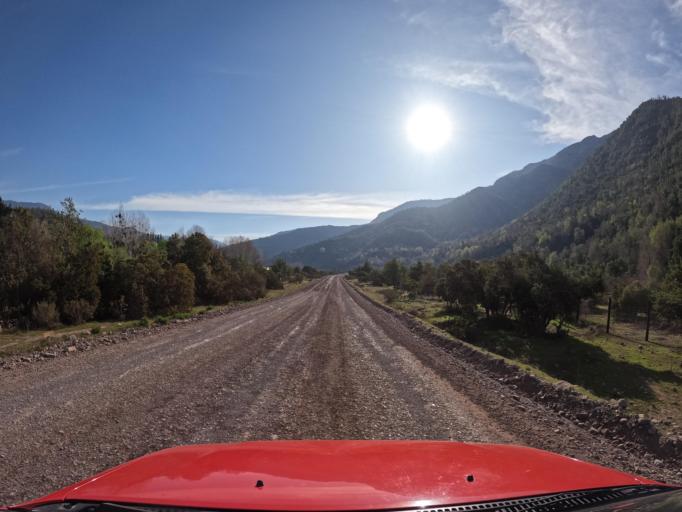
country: CL
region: O'Higgins
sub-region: Provincia de Colchagua
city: Chimbarongo
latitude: -34.9968
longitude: -70.8112
